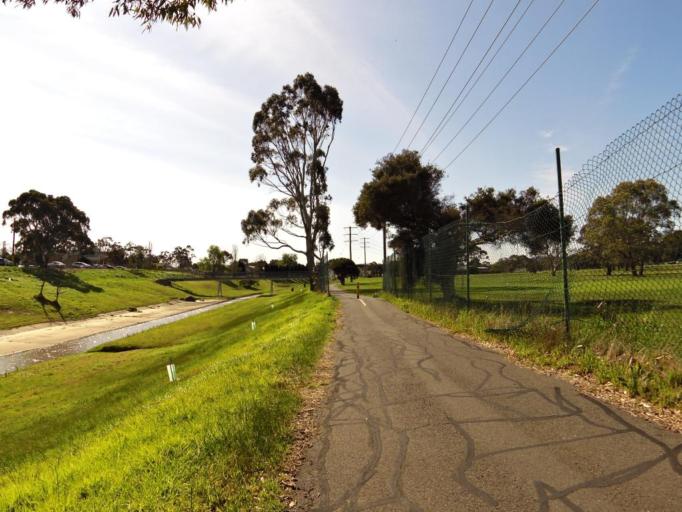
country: AU
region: Victoria
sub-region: Casey
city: Doveton
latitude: -37.9925
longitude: 145.2275
